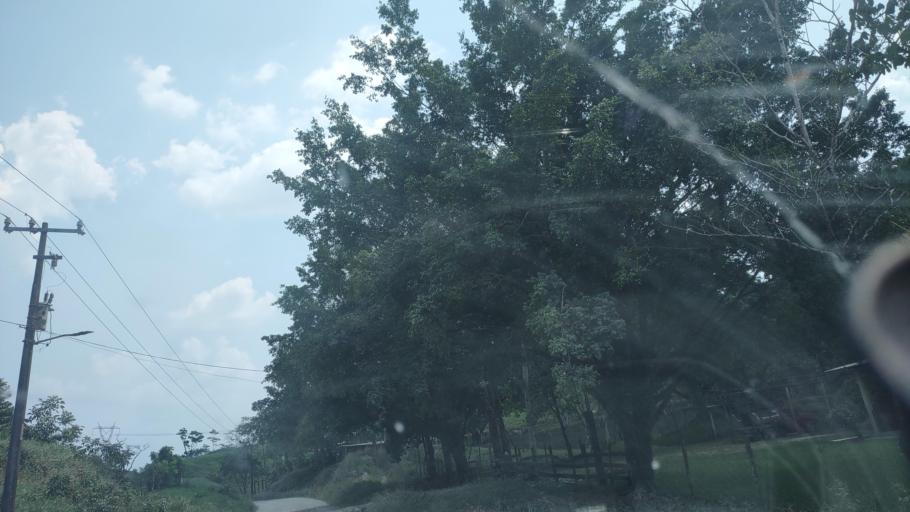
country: MX
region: Tabasco
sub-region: Huimanguillo
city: Francisco Rueda
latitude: 17.5978
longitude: -93.8998
